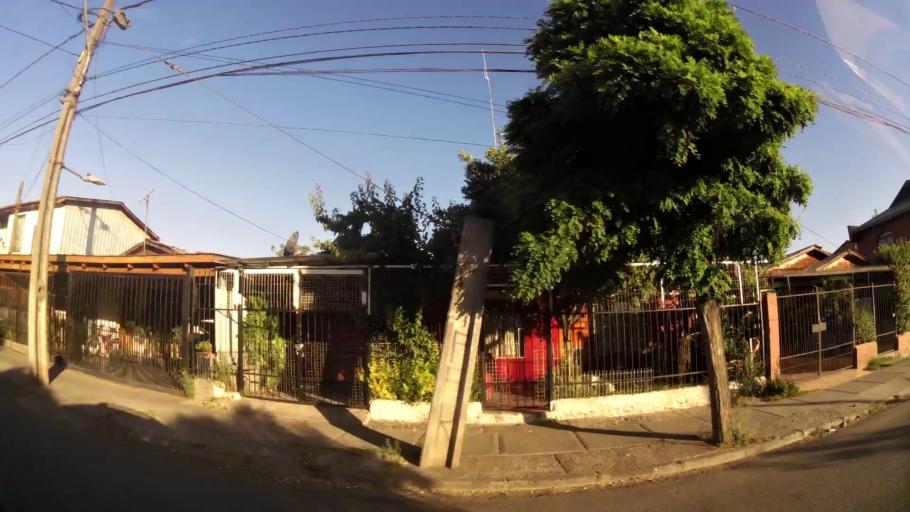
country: CL
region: Santiago Metropolitan
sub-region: Provincia de Maipo
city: San Bernardo
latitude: -33.5891
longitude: -70.6881
